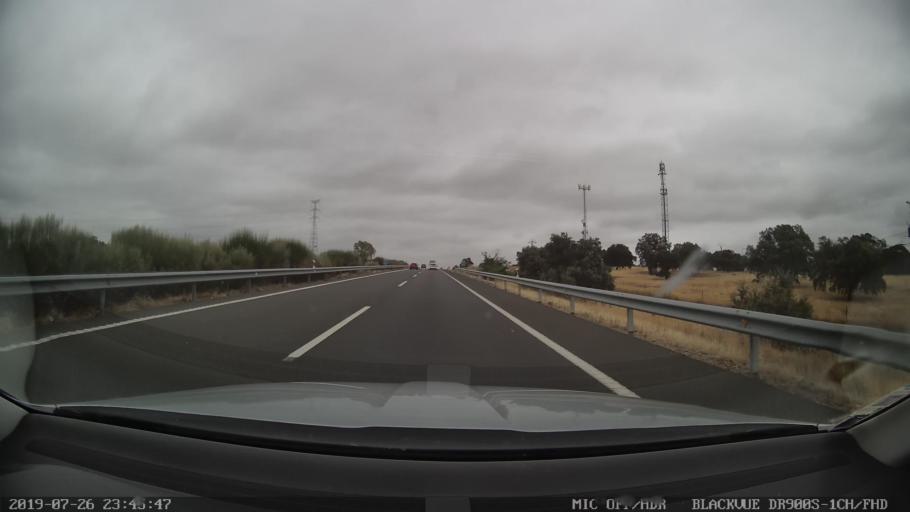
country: ES
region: Extremadura
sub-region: Provincia de Caceres
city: Torrecillas de la Tiesa
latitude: 39.5748
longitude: -5.8342
